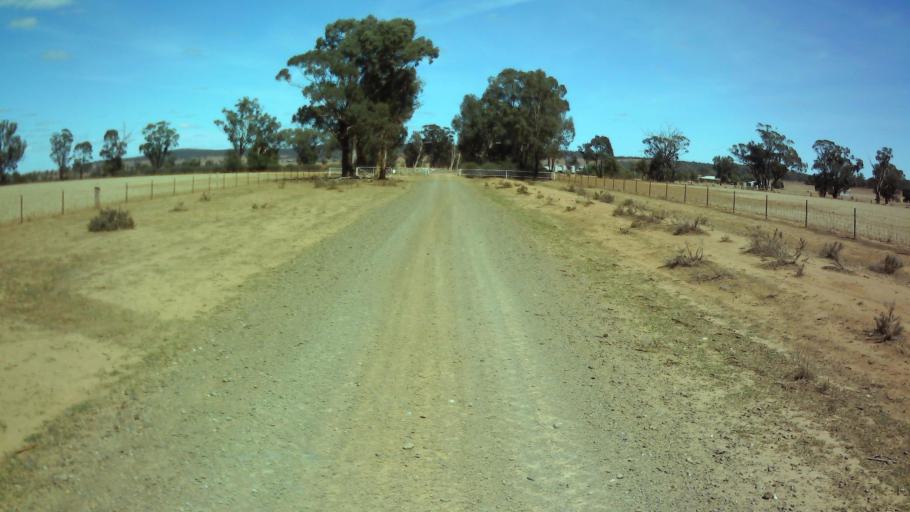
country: AU
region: New South Wales
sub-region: Forbes
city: Forbes
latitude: -33.7161
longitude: 147.8059
